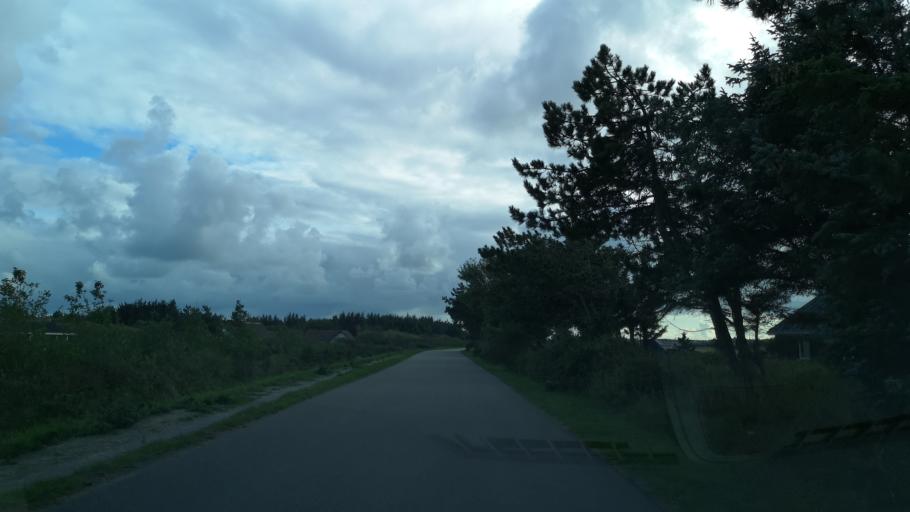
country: DK
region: Central Jutland
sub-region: Ringkobing-Skjern Kommune
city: Ringkobing
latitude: 56.1303
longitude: 8.1315
